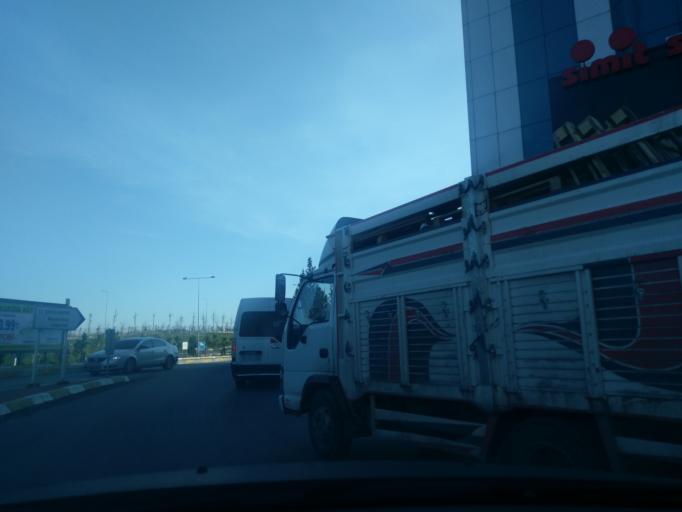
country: TR
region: Istanbul
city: Mahmutbey
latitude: 41.0707
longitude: 28.8197
